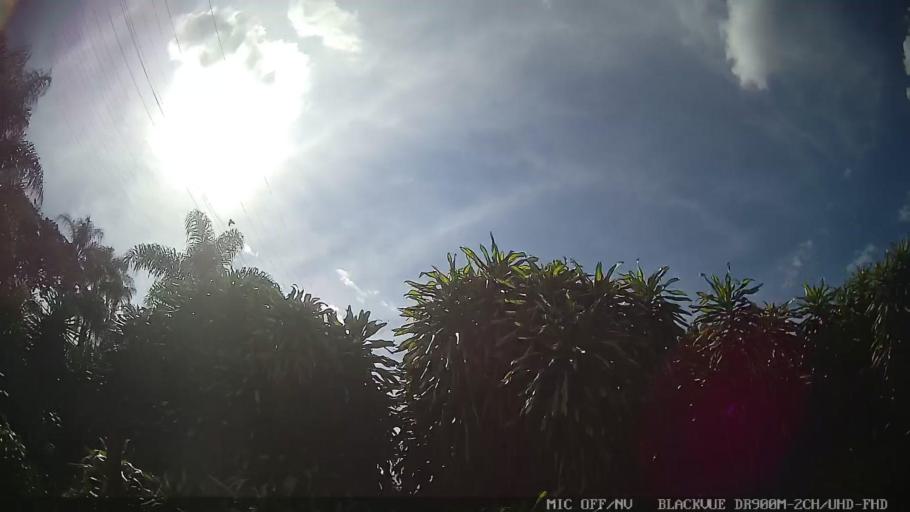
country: BR
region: Sao Paulo
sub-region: Cosmopolis
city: Cosmopolis
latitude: -22.6468
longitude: -47.0951
